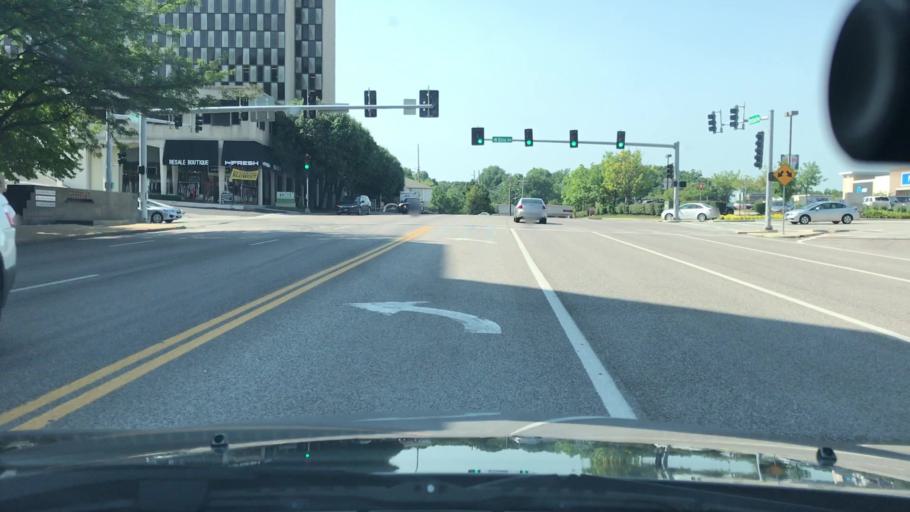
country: US
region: Missouri
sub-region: Saint Louis County
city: Brentwood
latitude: 38.6269
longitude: -90.3465
